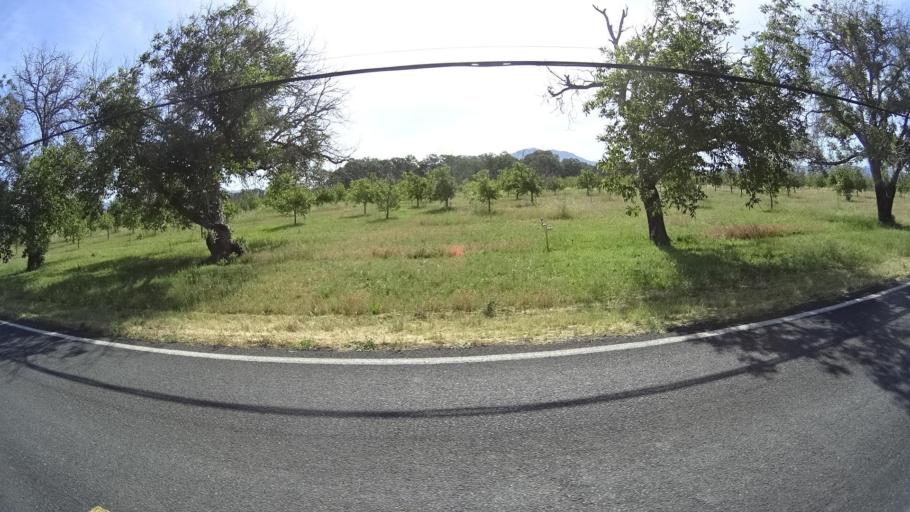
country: US
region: California
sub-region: Lake County
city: Kelseyville
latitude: 38.9895
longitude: -122.8942
